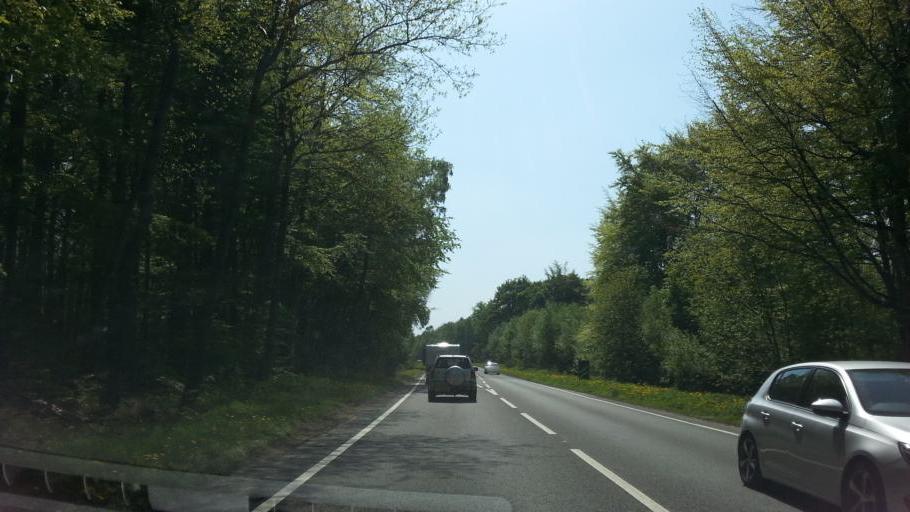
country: GB
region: England
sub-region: Nottinghamshire
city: Babworth
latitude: 53.2915
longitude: -1.0333
